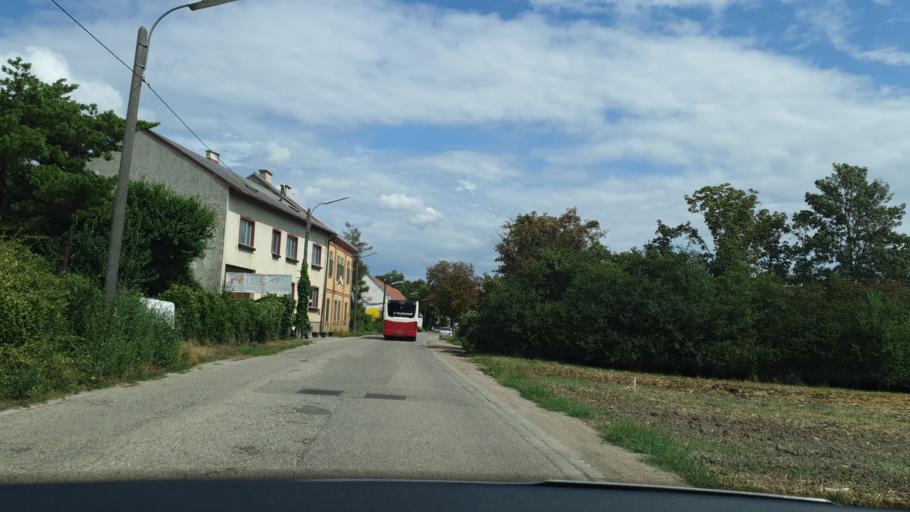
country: AT
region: Lower Austria
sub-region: Politischer Bezirk Wien-Umgebung
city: Leopoldsdorf
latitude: 48.1380
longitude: 16.3788
